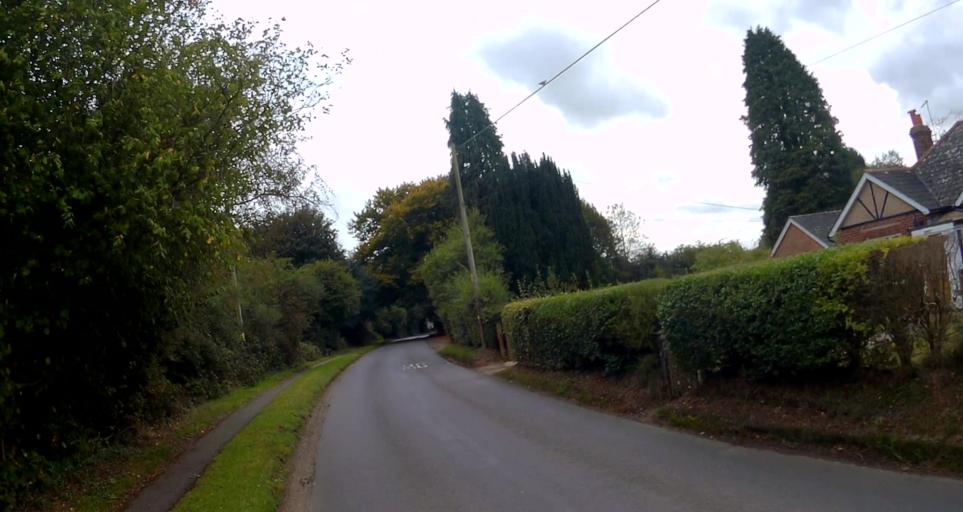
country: GB
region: England
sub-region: Hampshire
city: Four Marks
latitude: 51.1274
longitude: -1.0619
